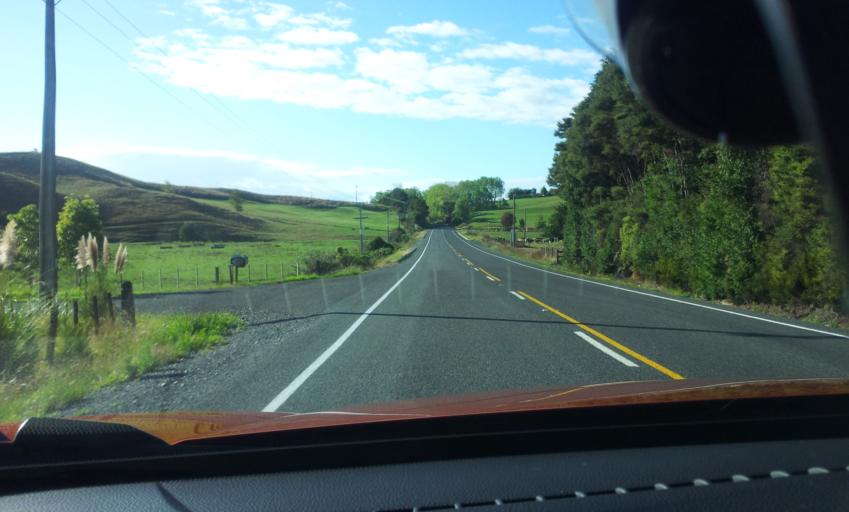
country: NZ
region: Waikato
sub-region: Hauraki District
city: Ngatea
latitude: -37.3110
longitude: 175.3829
